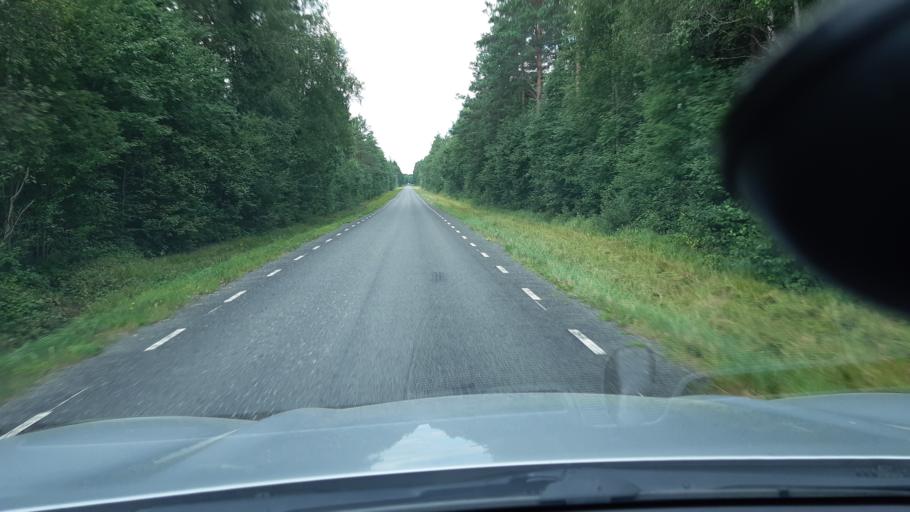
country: EE
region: Raplamaa
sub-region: Jaervakandi vald
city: Jarvakandi
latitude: 58.8667
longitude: 24.7735
